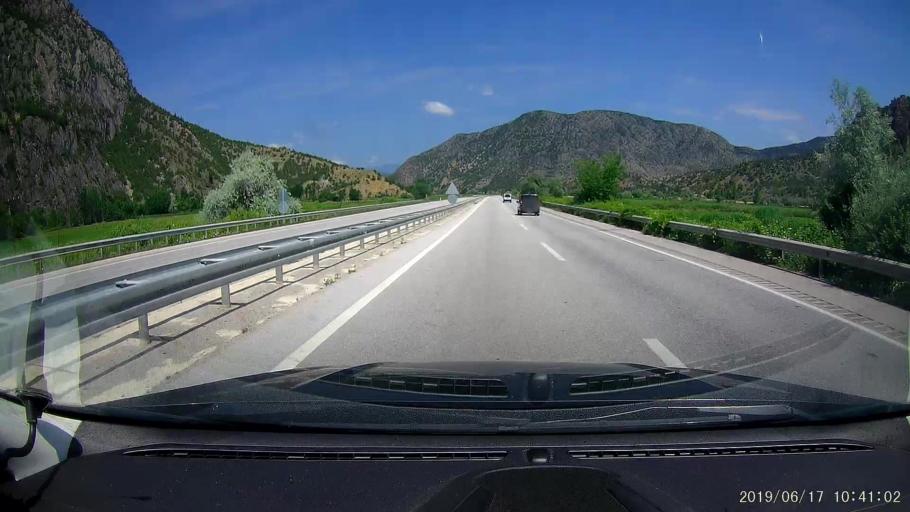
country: TR
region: Corum
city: Kargi
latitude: 41.0336
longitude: 34.5848
